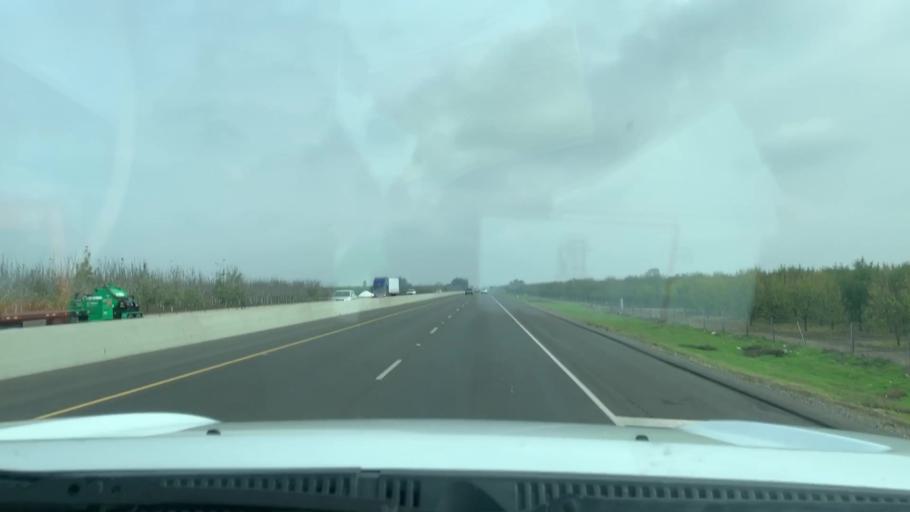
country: US
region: California
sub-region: Kings County
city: Armona
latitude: 36.3015
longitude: -119.7392
